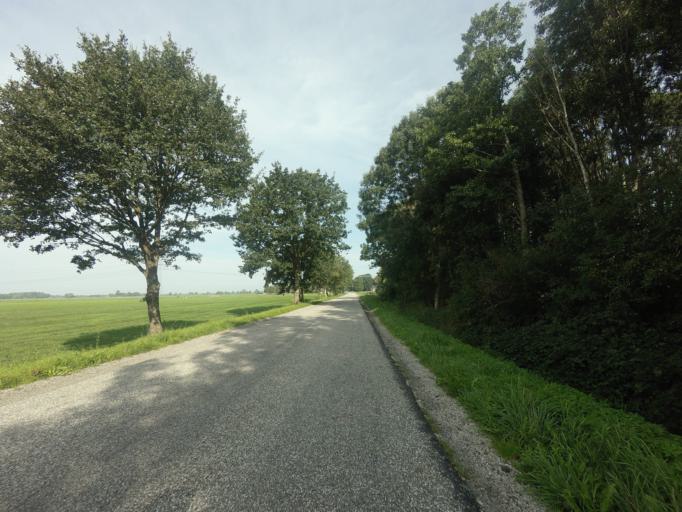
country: NL
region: Groningen
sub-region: Gemeente Leek
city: Leek
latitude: 53.1933
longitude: 6.3544
